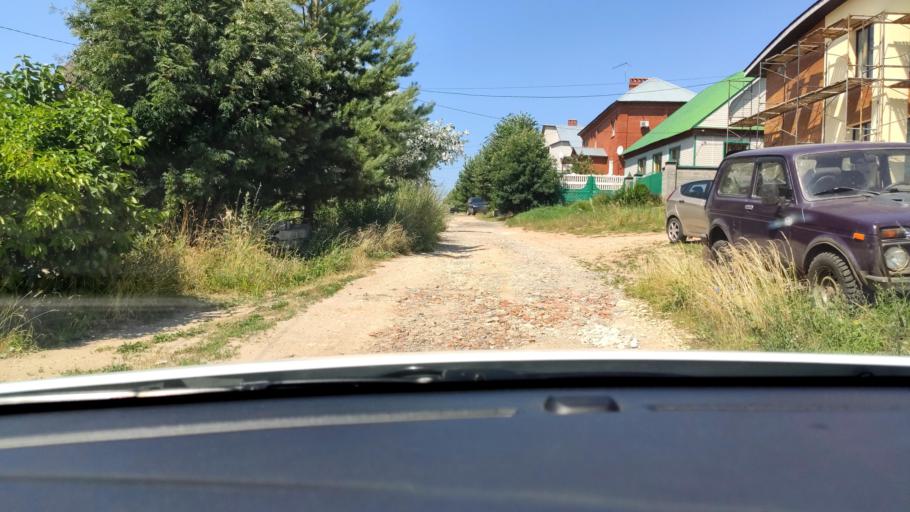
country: RU
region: Tatarstan
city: Stolbishchi
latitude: 55.7536
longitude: 49.2928
